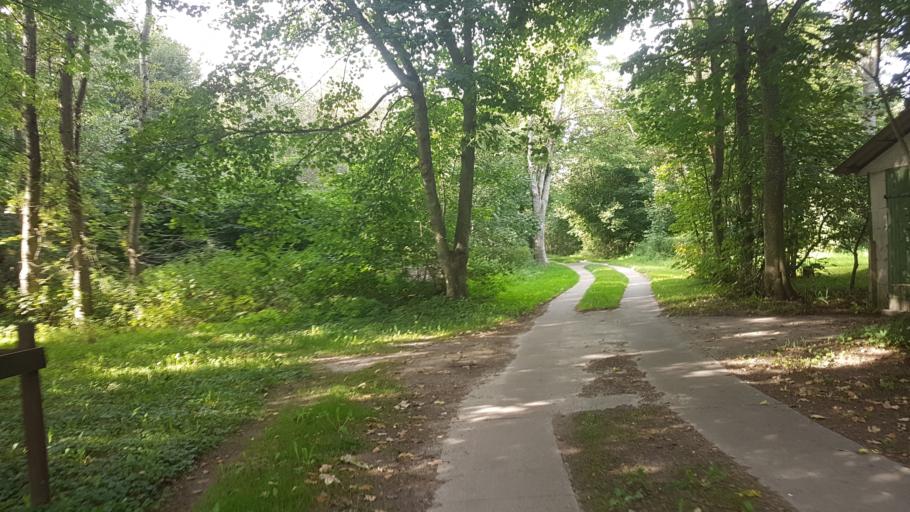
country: DE
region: Mecklenburg-Vorpommern
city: Gingst
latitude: 54.4417
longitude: 13.1855
